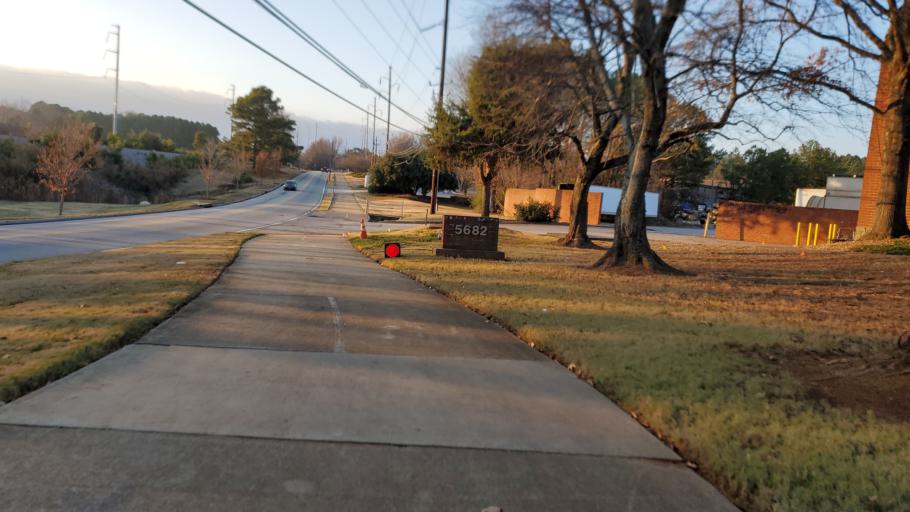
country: US
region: Georgia
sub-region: DeKalb County
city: Stone Mountain
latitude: 33.8225
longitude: -84.1877
